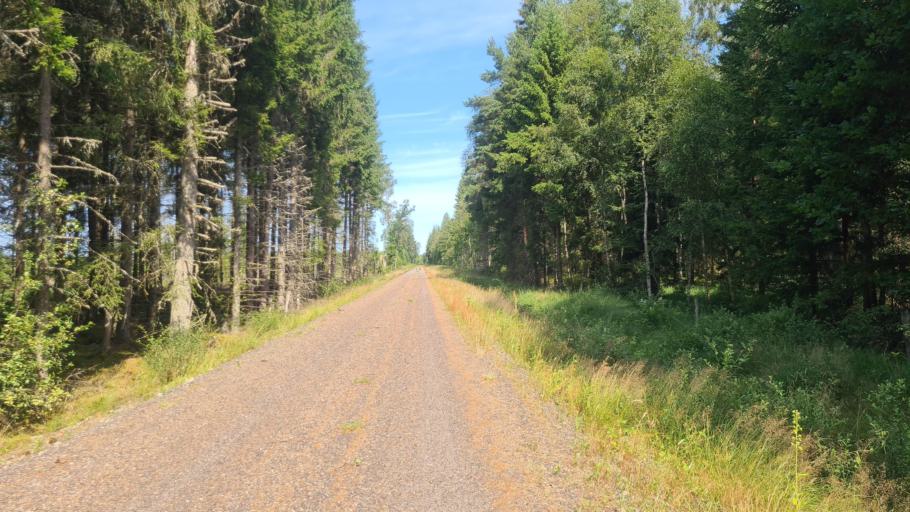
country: SE
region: Kronoberg
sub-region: Ljungby Kommun
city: Lagan
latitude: 56.9795
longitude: 13.9467
